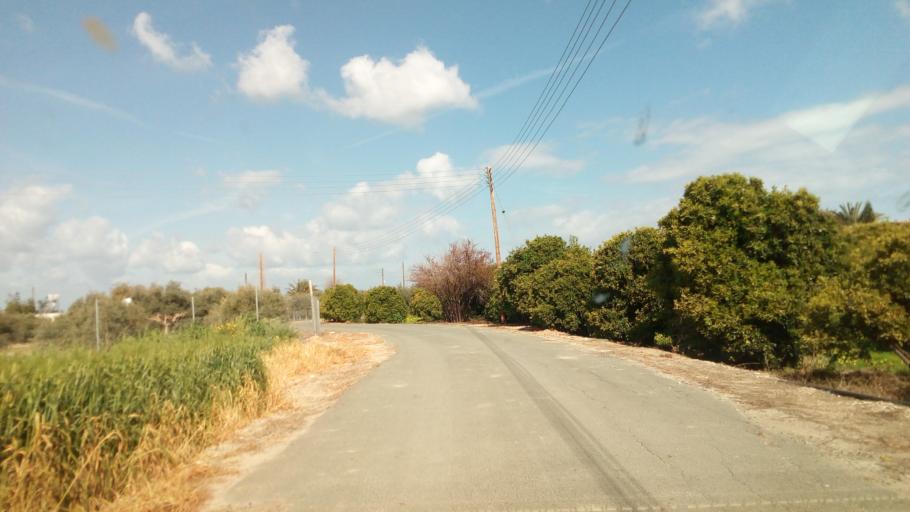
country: CY
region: Pafos
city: Polis
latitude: 35.0301
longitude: 32.4230
